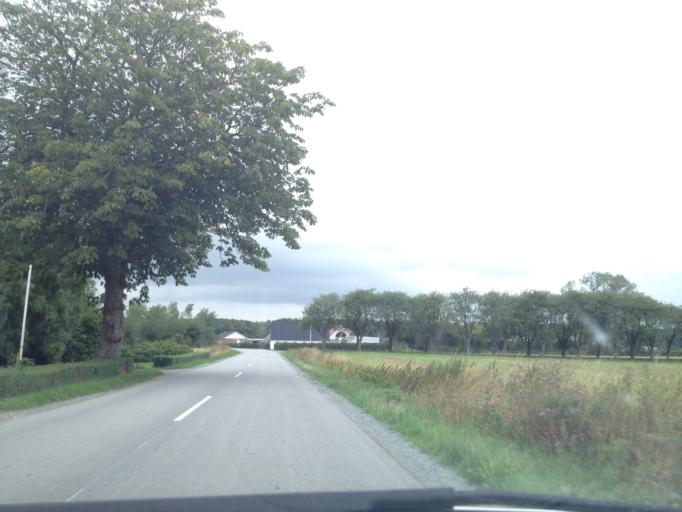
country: DK
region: South Denmark
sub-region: Haderslev Kommune
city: Starup
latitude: 55.3051
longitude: 9.5411
